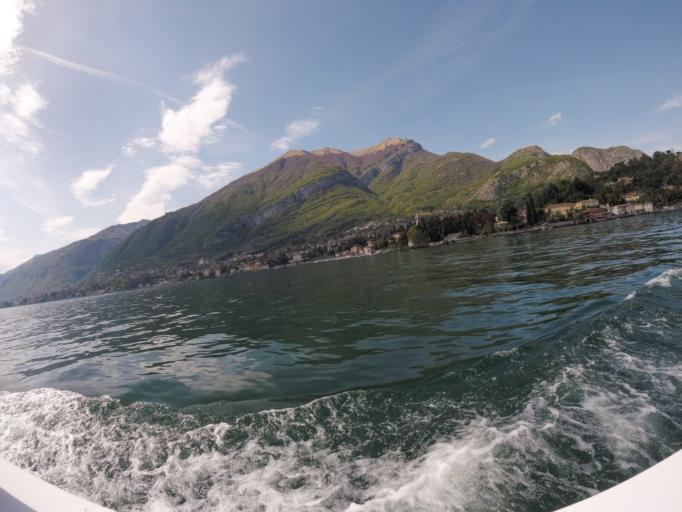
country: IT
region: Lombardy
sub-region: Provincia di Como
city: Tremezzo
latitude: 45.9787
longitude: 9.2230
